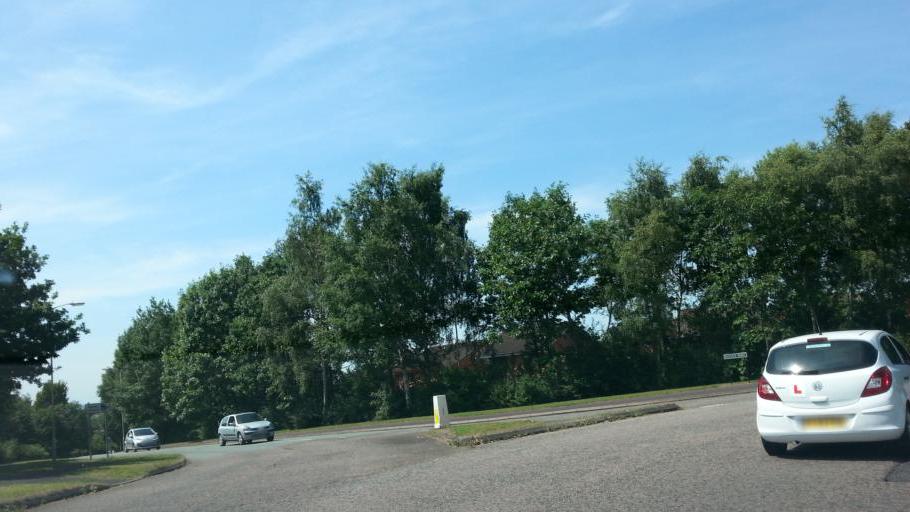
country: GB
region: England
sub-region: Staffordshire
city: Great Wyrley
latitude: 52.6904
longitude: -1.9995
